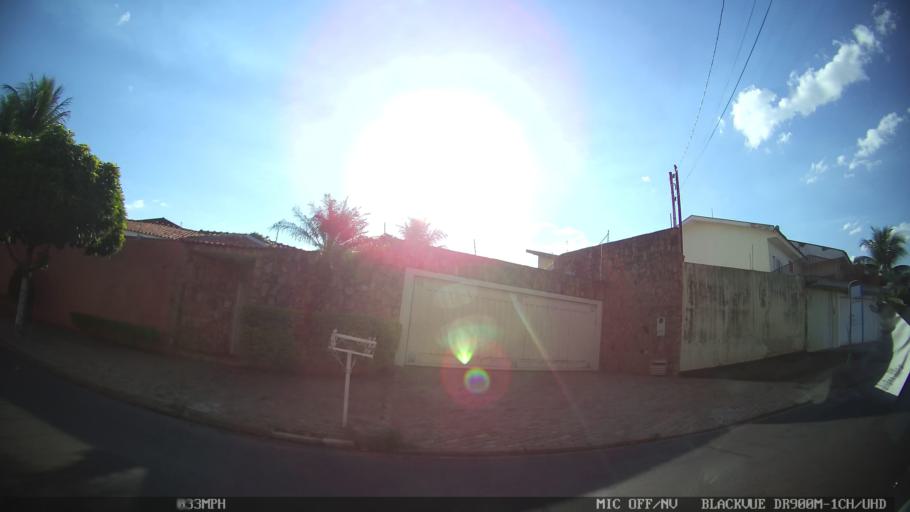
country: BR
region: Sao Paulo
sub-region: Ribeirao Preto
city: Ribeirao Preto
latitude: -21.2057
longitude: -47.7759
